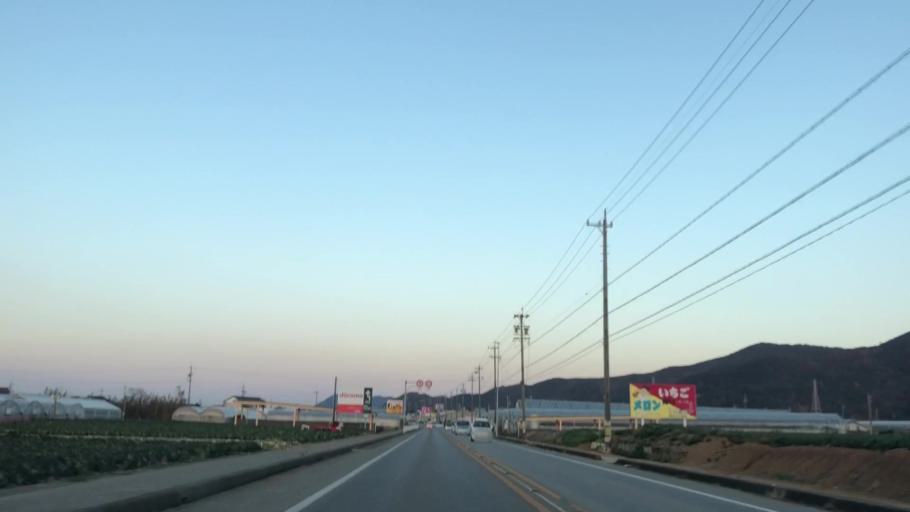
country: JP
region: Aichi
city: Tahara
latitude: 34.6283
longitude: 137.1115
